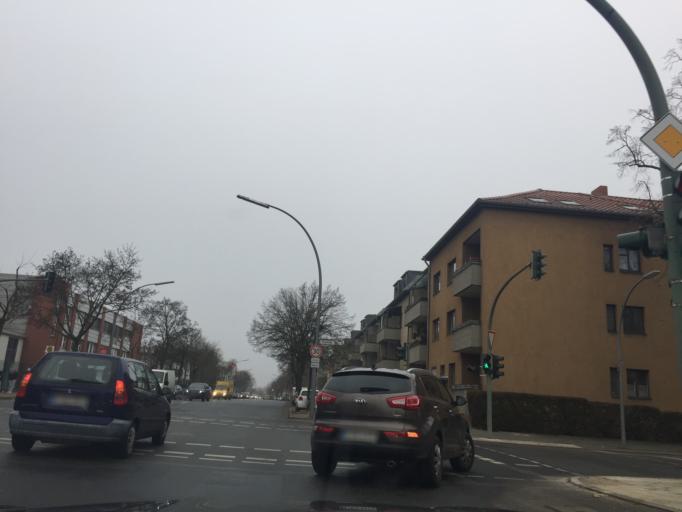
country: DE
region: Berlin
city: Wittenau
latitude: 52.5841
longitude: 13.3097
